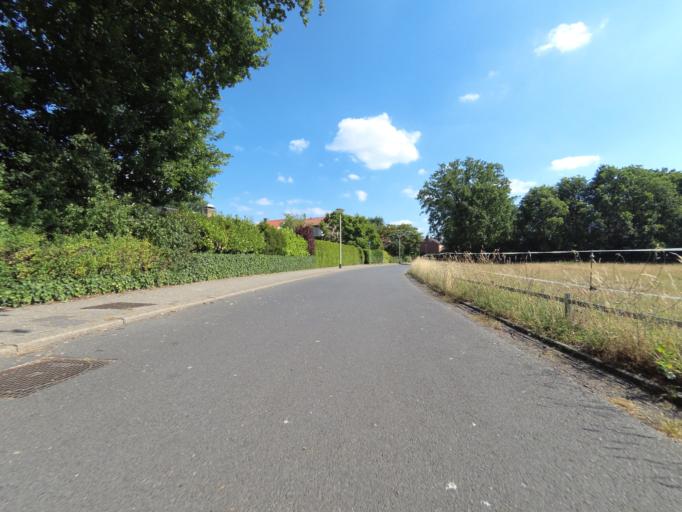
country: NL
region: Overijssel
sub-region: Gemeente Oldenzaal
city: Oldenzaal
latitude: 52.3260
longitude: 6.9203
